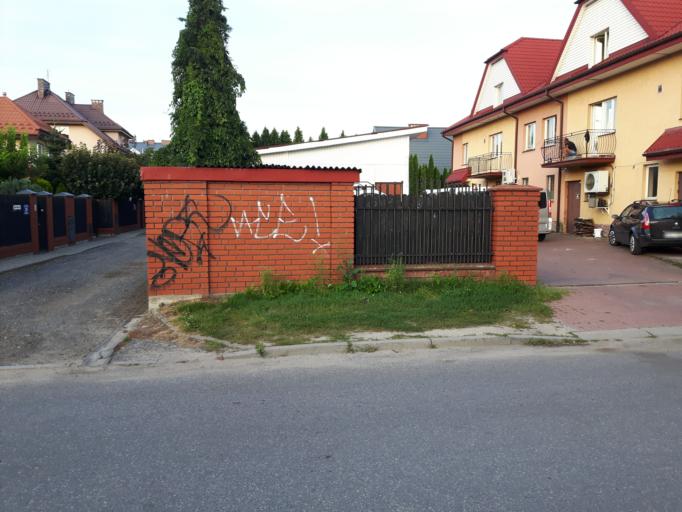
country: PL
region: Masovian Voivodeship
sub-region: Powiat wolominski
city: Zabki
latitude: 52.2846
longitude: 21.1219
